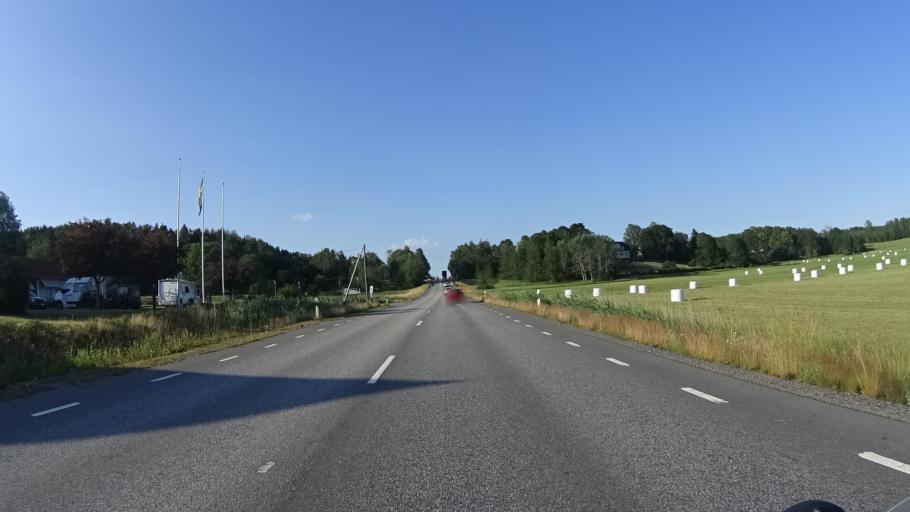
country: SE
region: Stockholm
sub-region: Sodertalje Kommun
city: Pershagen
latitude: 59.0863
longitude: 17.6103
